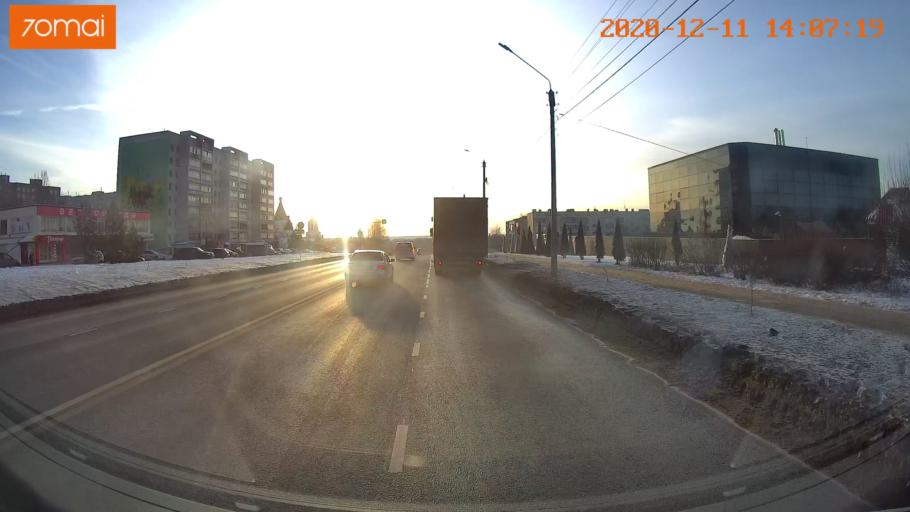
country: RU
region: Kostroma
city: Oktyabr'skiy
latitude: 57.7384
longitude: 40.9994
